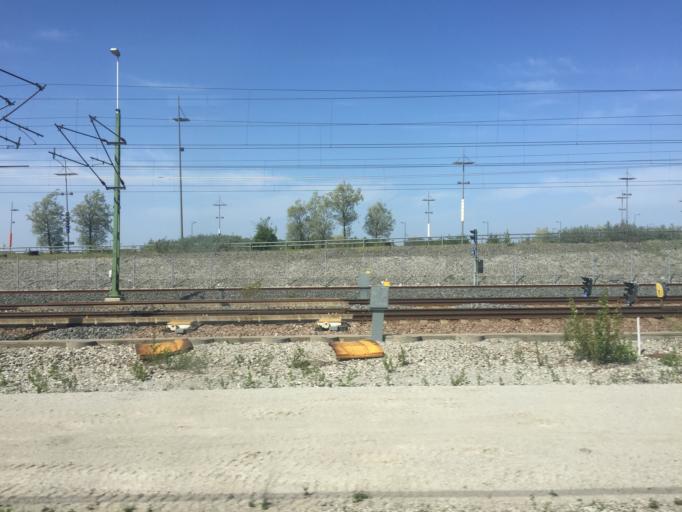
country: SE
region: Skane
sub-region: Malmo
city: Bunkeflostrand
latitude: 55.5606
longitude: 12.9703
